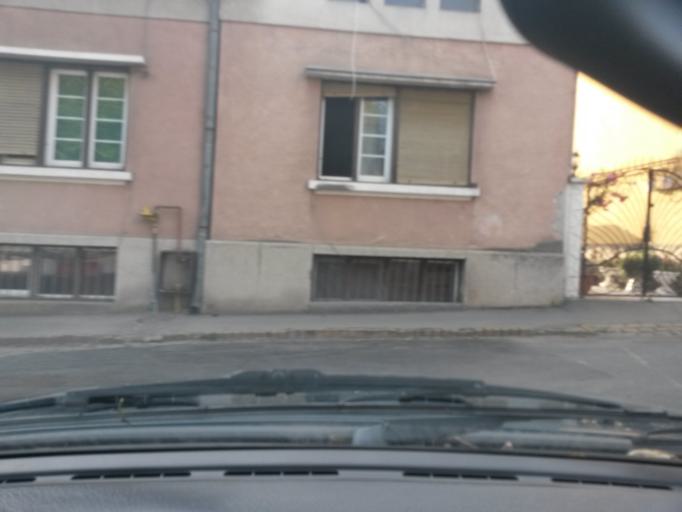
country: RO
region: Mures
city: Targu-Mures
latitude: 46.5485
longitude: 24.5656
